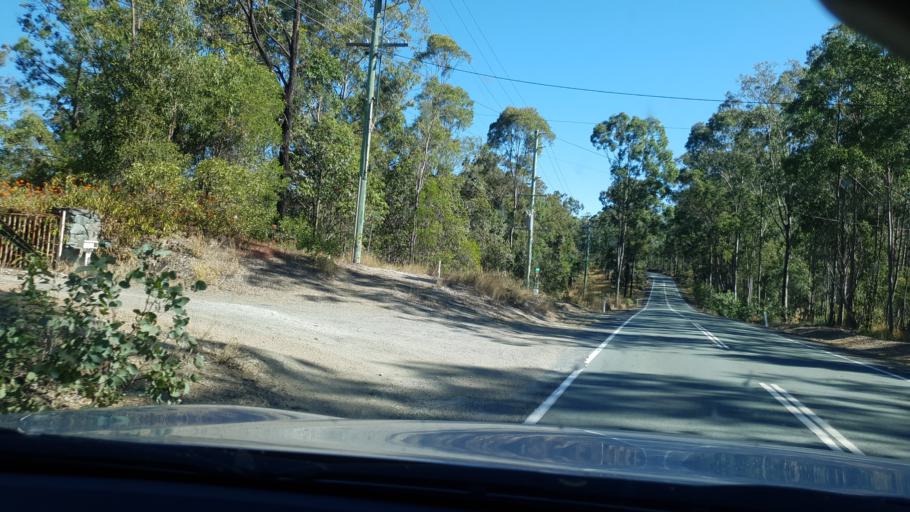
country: AU
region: Queensland
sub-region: Moreton Bay
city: Strathpine
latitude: -27.3282
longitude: 152.9334
